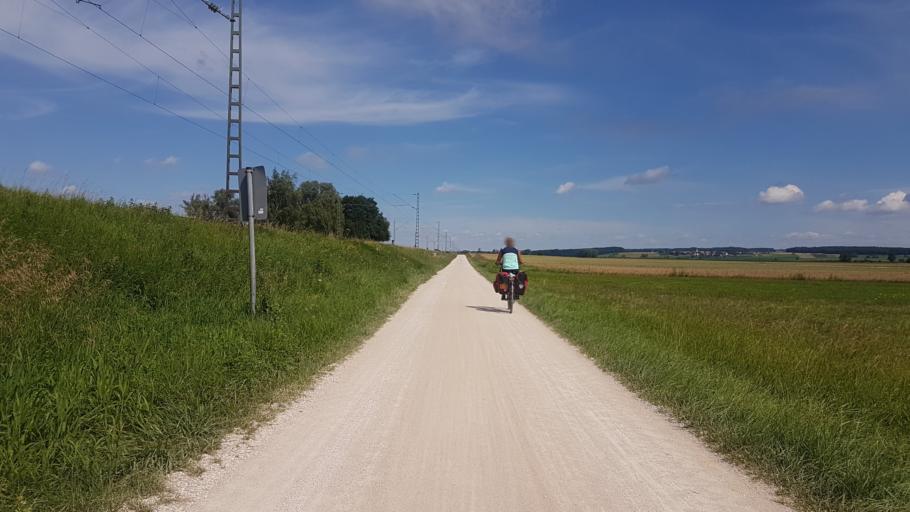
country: DE
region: Bavaria
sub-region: Regierungsbezirk Mittelfranken
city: Markt Berolzheim
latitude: 49.0241
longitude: 10.8477
